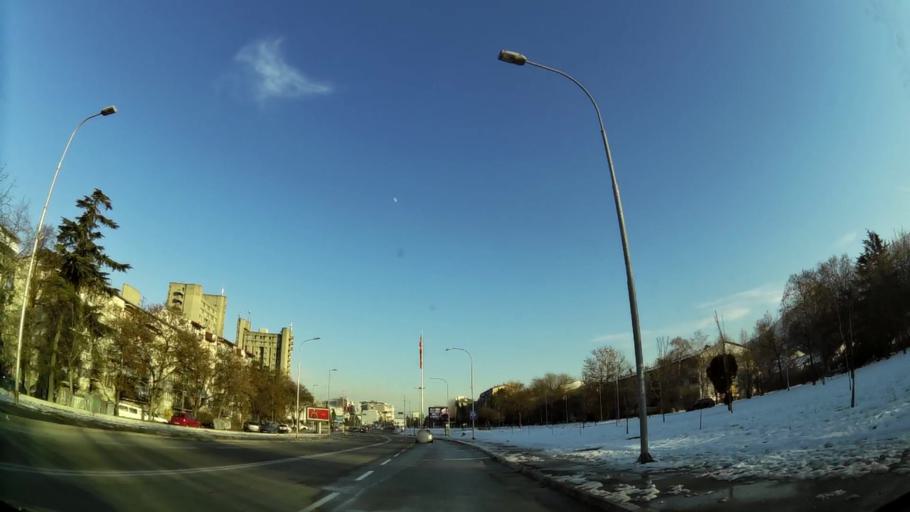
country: MK
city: Krushopek
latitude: 41.9985
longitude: 21.3876
